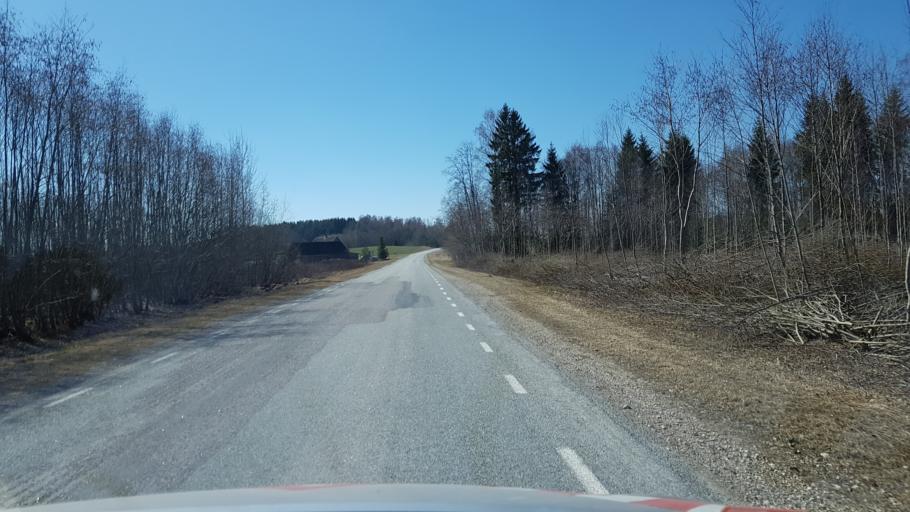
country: EE
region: Laeaene-Virumaa
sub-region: Rakke vald
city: Rakke
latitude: 59.0104
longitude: 26.3348
